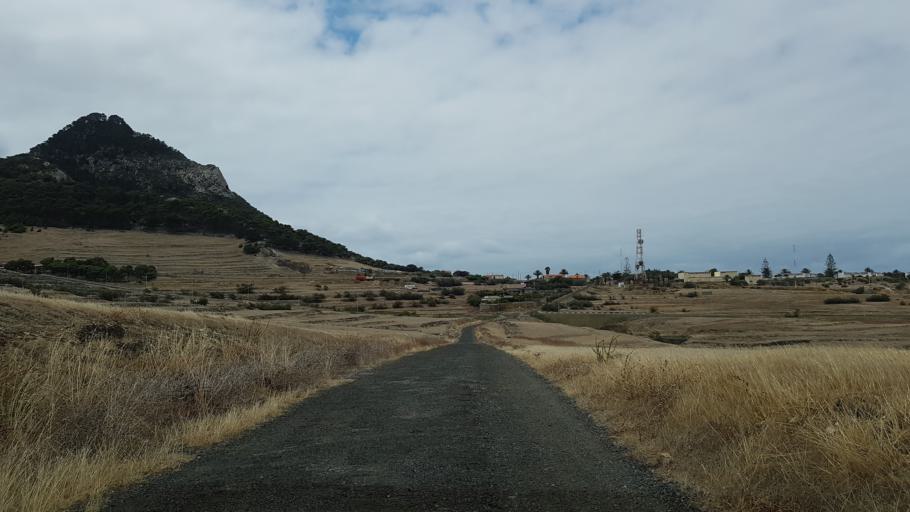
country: PT
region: Madeira
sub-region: Porto Santo
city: Camacha
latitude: 33.0912
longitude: -16.3359
